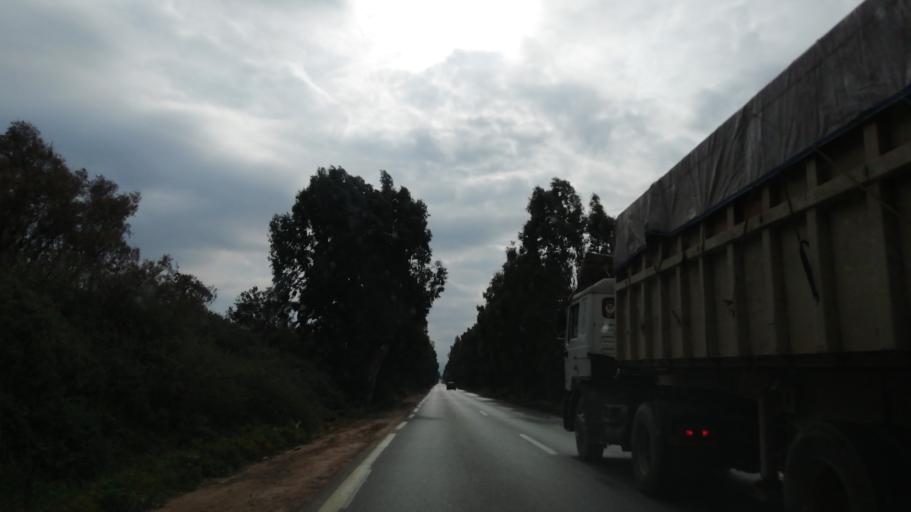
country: DZ
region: Oran
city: Sidi ech Chahmi
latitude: 35.5841
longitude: -0.4529
